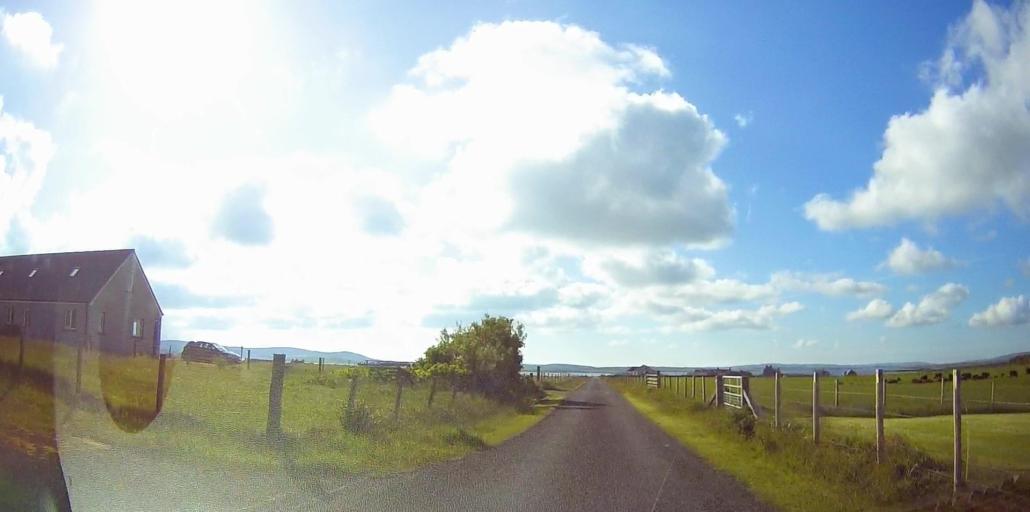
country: GB
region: Scotland
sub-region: Orkney Islands
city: Stromness
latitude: 58.9864
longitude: -3.1925
